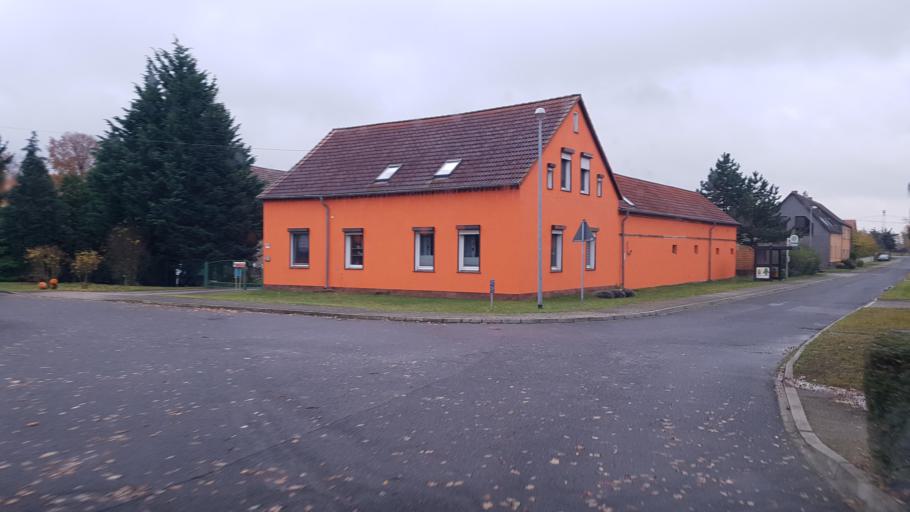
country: DE
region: Brandenburg
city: Drebkau
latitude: 51.6634
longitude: 14.2514
